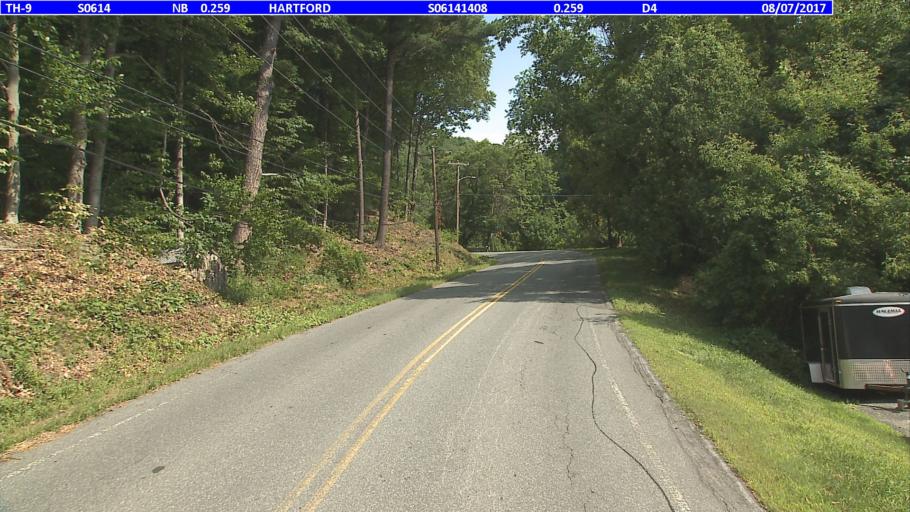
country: US
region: Vermont
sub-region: Windsor County
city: White River Junction
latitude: 43.6617
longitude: -72.3341
